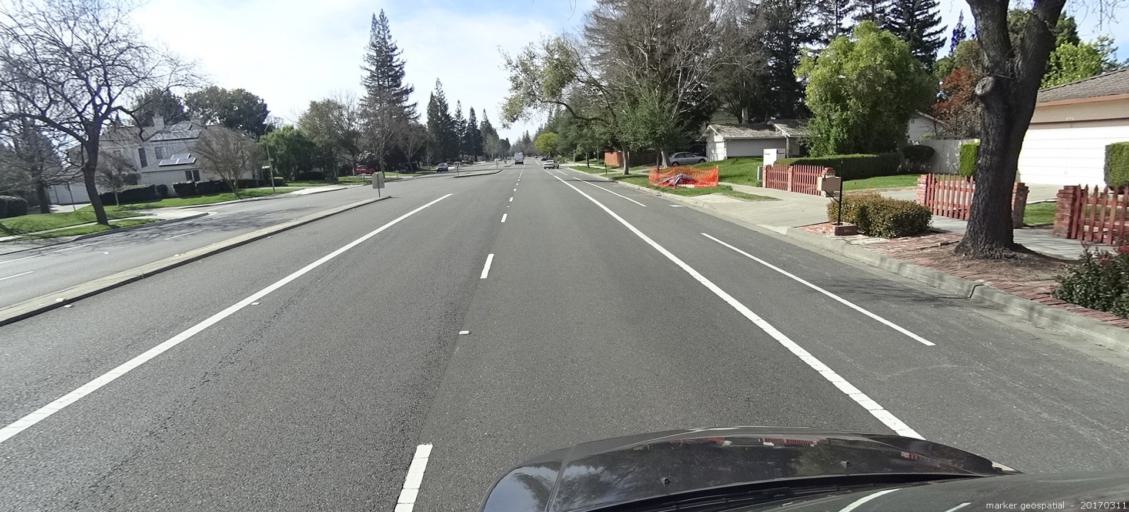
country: US
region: California
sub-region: Yolo County
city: West Sacramento
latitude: 38.5009
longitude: -121.5493
